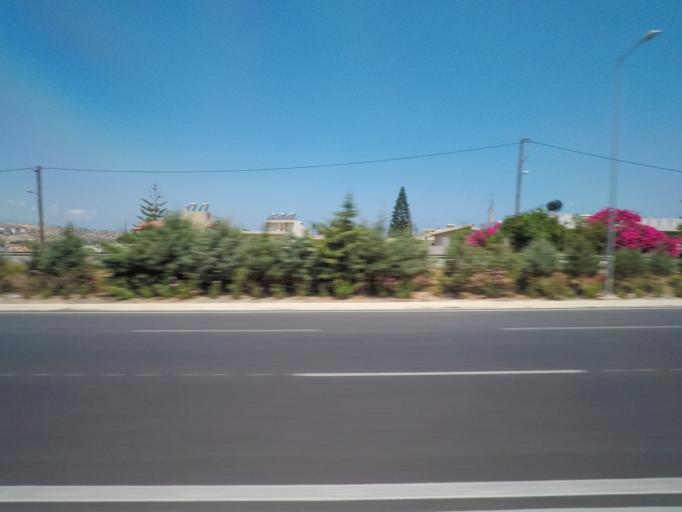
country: GR
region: Crete
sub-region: Nomos Irakleiou
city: Nea Alikarnassos
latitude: 35.3268
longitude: 25.2026
